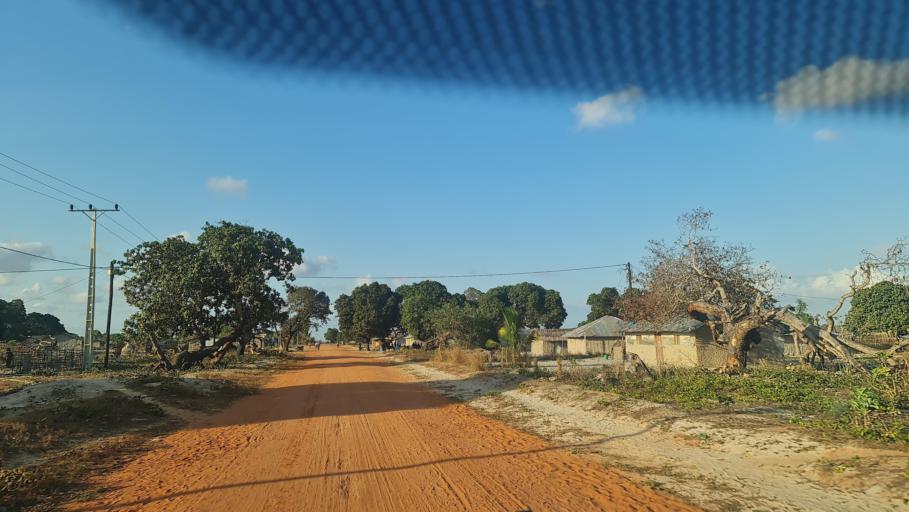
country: MZ
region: Nampula
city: Ilha de Mocambique
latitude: -14.8442
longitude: 40.7665
